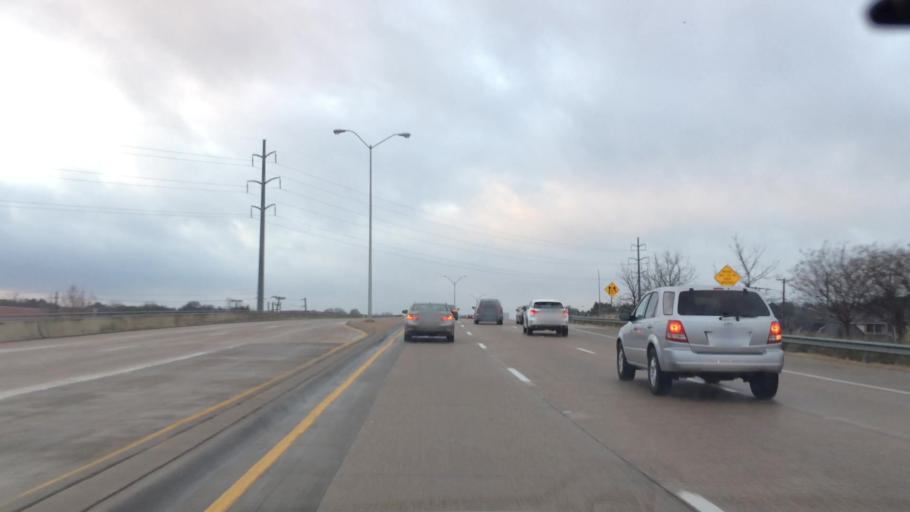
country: US
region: Texas
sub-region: Dallas County
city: Addison
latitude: 32.9722
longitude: -96.8041
